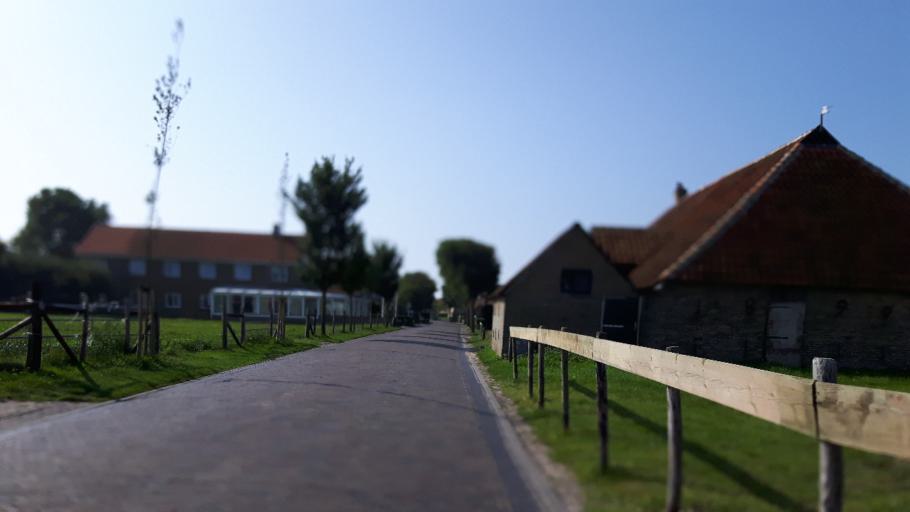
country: NL
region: Friesland
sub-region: Gemeente Ameland
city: Nes
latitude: 53.4505
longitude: 5.8007
